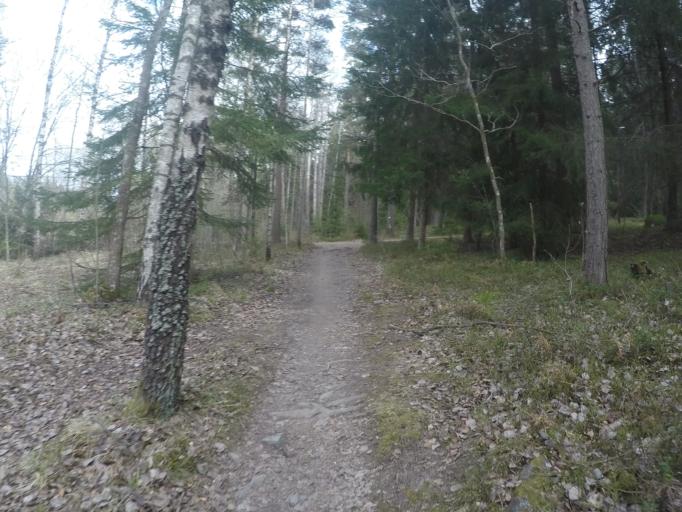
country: SE
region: Vaestmanland
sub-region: Vasteras
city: Vasteras
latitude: 59.6295
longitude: 16.5171
